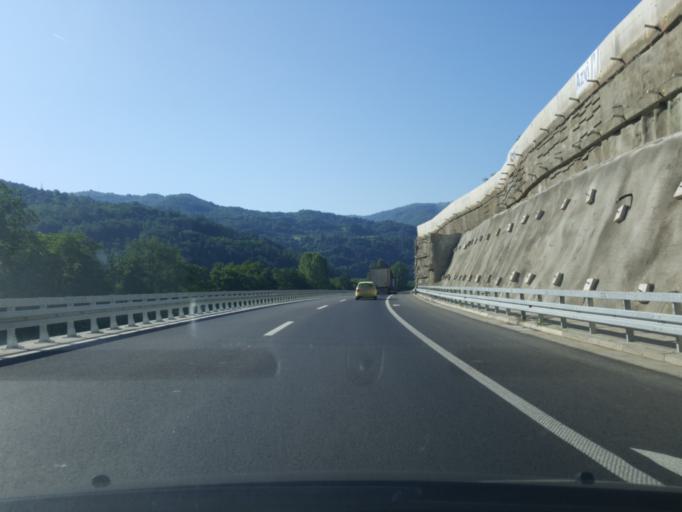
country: RS
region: Central Serbia
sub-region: Jablanicki Okrug
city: Vlasotince
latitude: 42.8532
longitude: 22.1257
